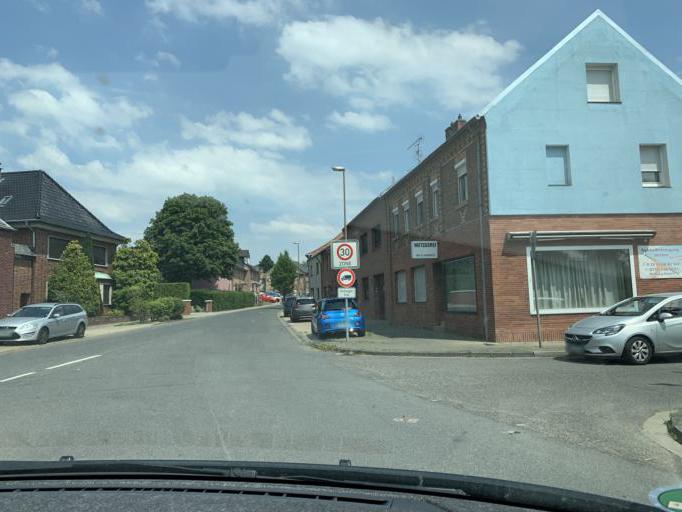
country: DE
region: North Rhine-Westphalia
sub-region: Regierungsbezirk Koln
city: Bedburg
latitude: 50.9823
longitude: 6.5157
